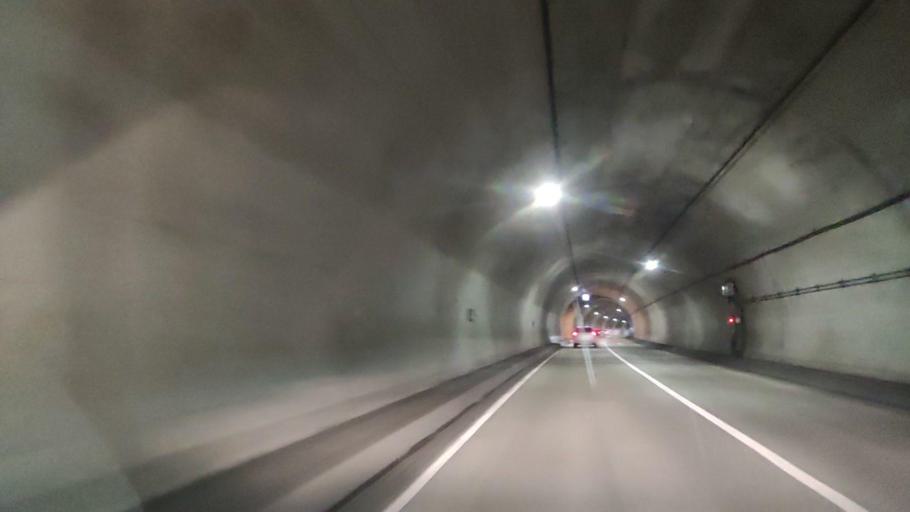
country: JP
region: Hokkaido
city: Ishikari
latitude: 43.5256
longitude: 141.3937
